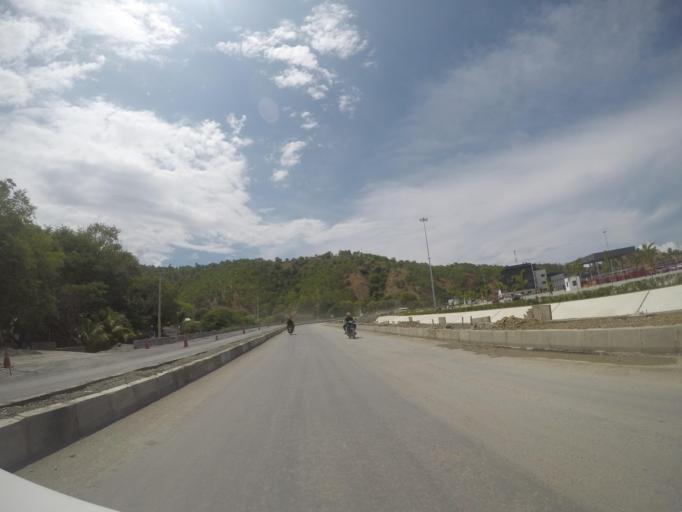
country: TL
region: Dili
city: Dili
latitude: -8.5753
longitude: 125.4742
